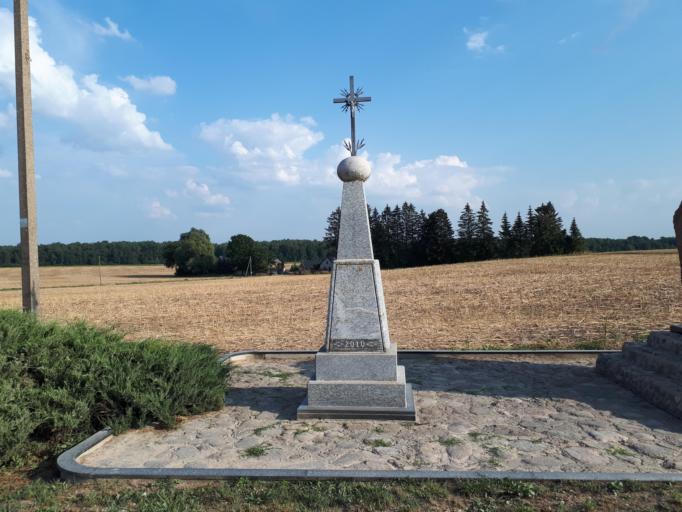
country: LT
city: Vabalninkas
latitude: 55.9144
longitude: 24.8536
